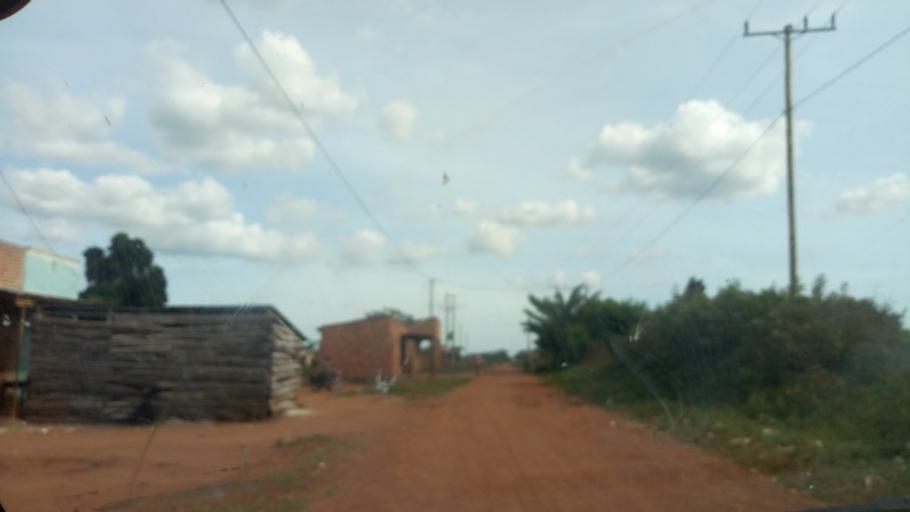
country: UG
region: Western Region
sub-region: Kiryandongo District
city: Kiryandongo
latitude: 1.8105
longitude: 31.9415
